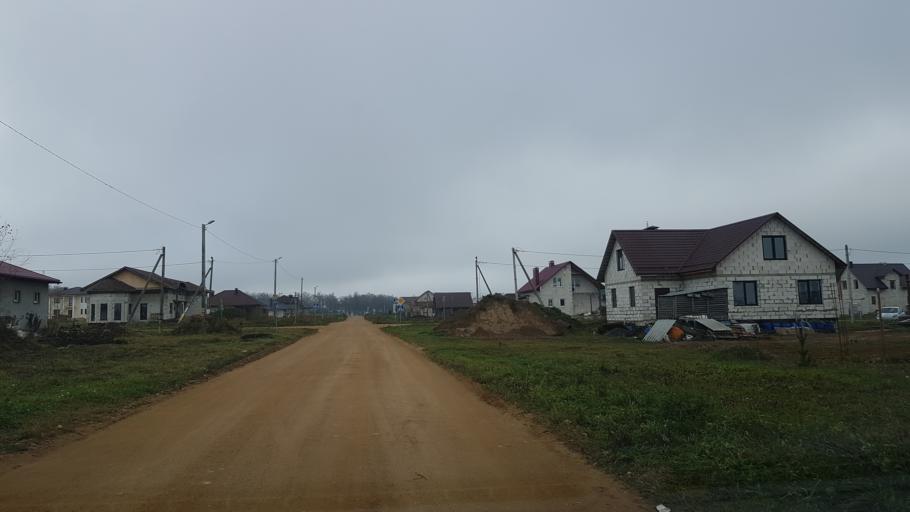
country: BY
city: Fanipol
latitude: 53.7308
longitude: 27.3245
